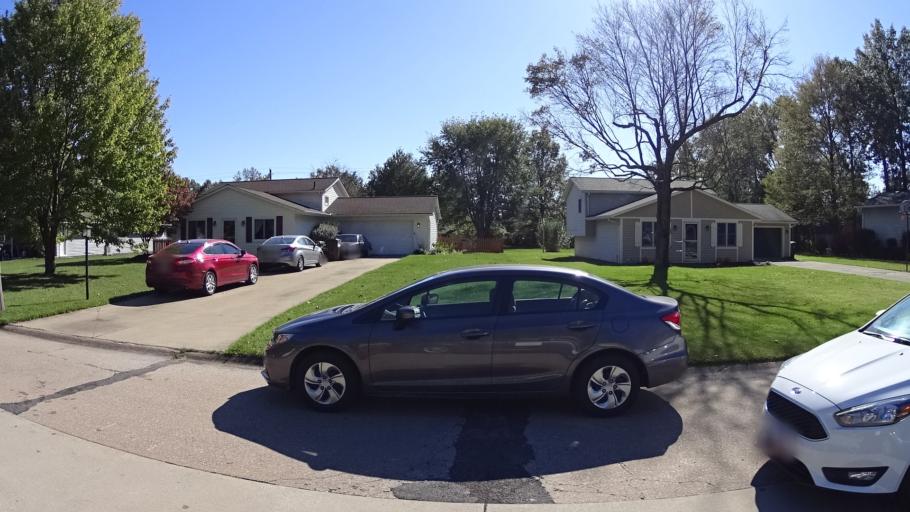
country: US
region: Ohio
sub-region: Lorain County
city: Amherst
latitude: 41.4042
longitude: -82.1937
